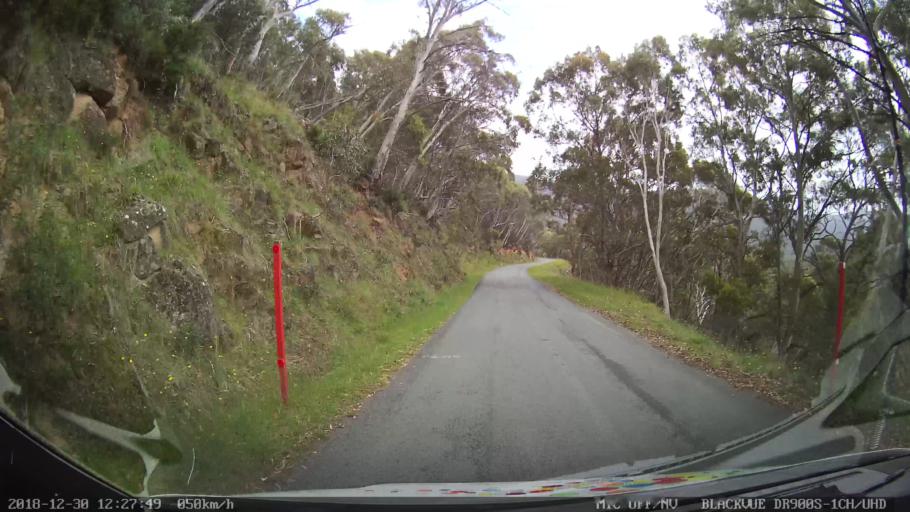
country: AU
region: New South Wales
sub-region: Snowy River
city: Jindabyne
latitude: -36.3285
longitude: 148.4892
